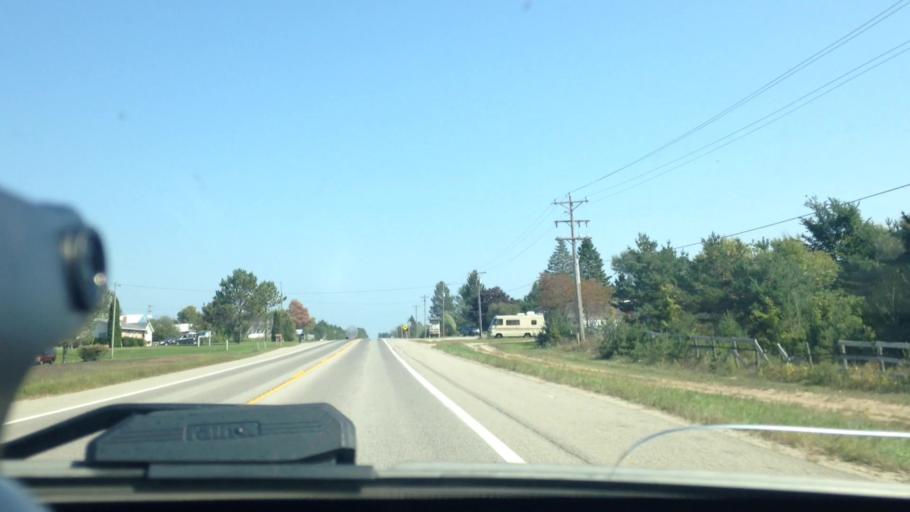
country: US
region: Michigan
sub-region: Luce County
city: Newberry
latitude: 46.3032
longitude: -85.5014
